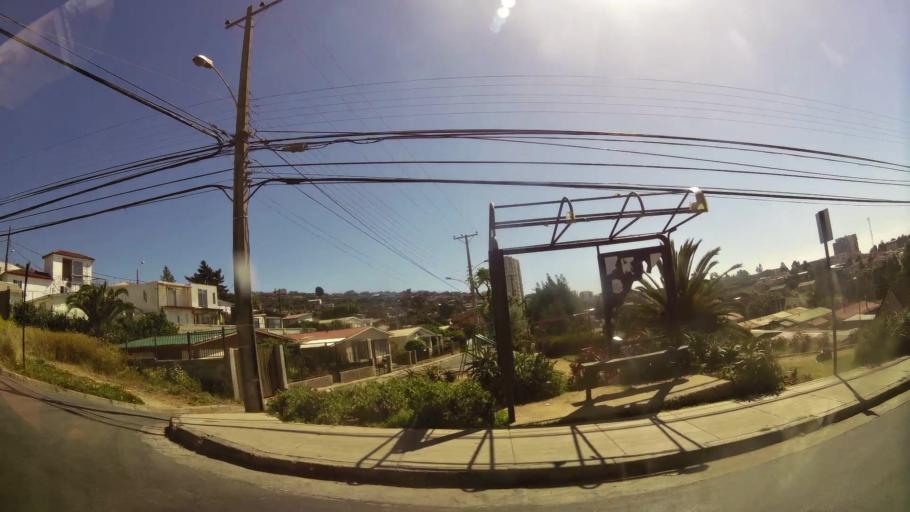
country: CL
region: Valparaiso
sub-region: Provincia de Valparaiso
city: Vina del Mar
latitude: -33.0343
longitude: -71.5744
